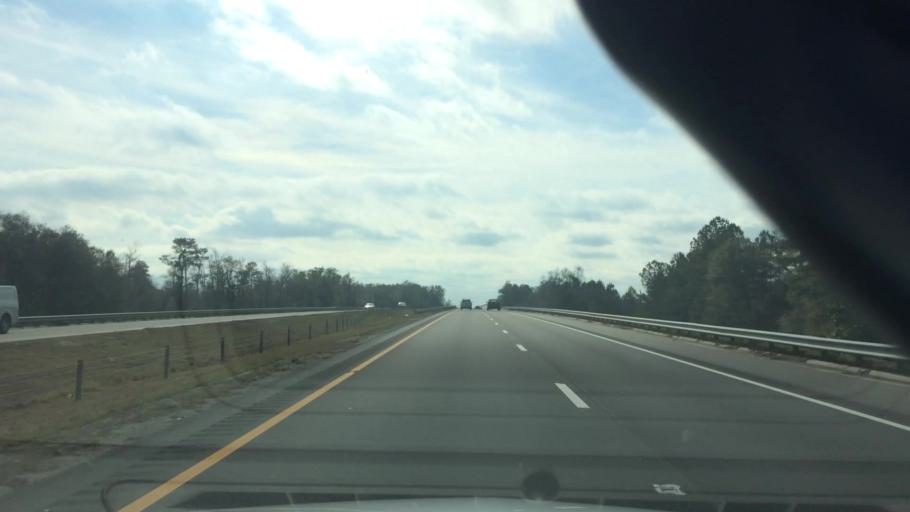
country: US
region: North Carolina
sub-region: New Hanover County
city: Wrightsboro
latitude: 34.3108
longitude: -77.9493
